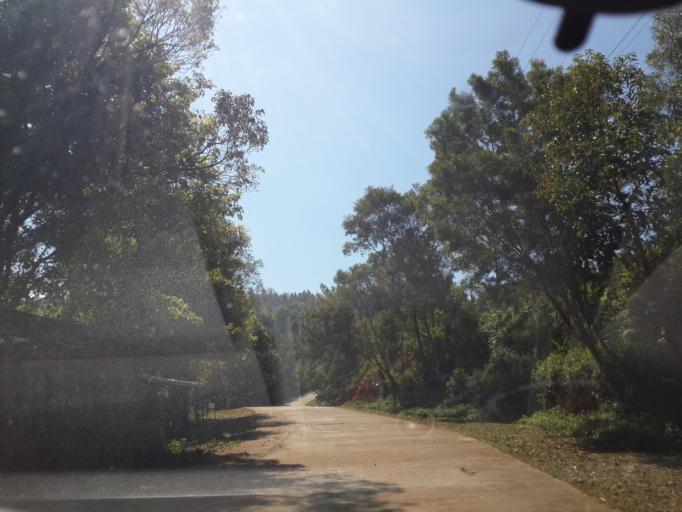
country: TH
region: Chiang Mai
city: Fang
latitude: 19.9214
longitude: 99.0506
